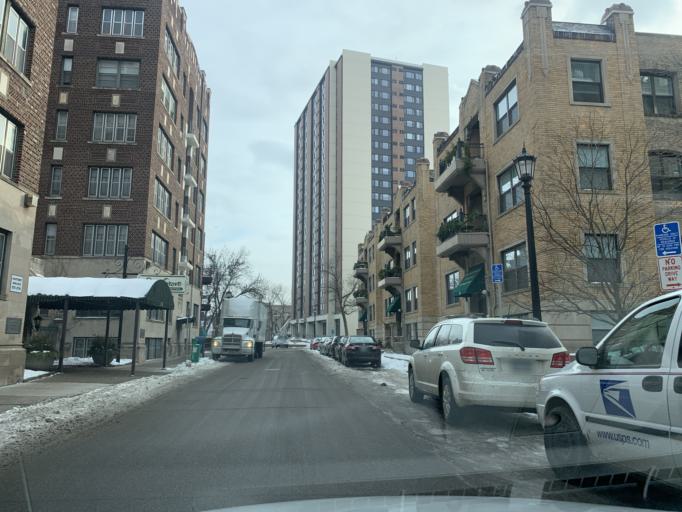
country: US
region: Minnesota
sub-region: Hennepin County
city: Minneapolis
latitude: 44.9668
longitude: -93.2827
